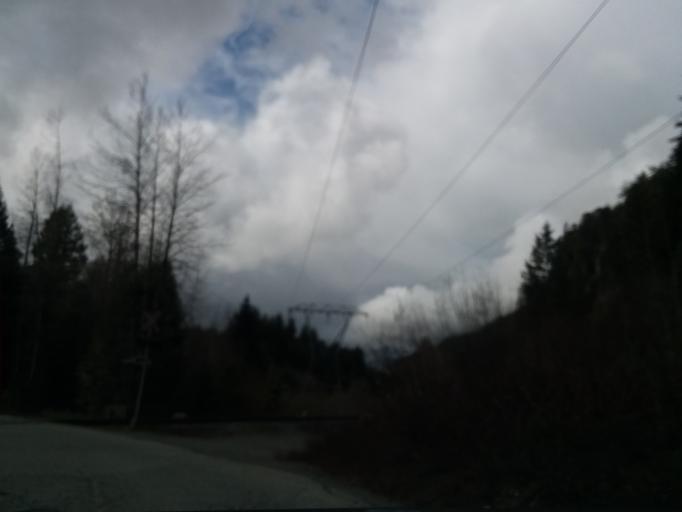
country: CA
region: British Columbia
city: Whistler
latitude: 50.0944
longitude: -123.0128
